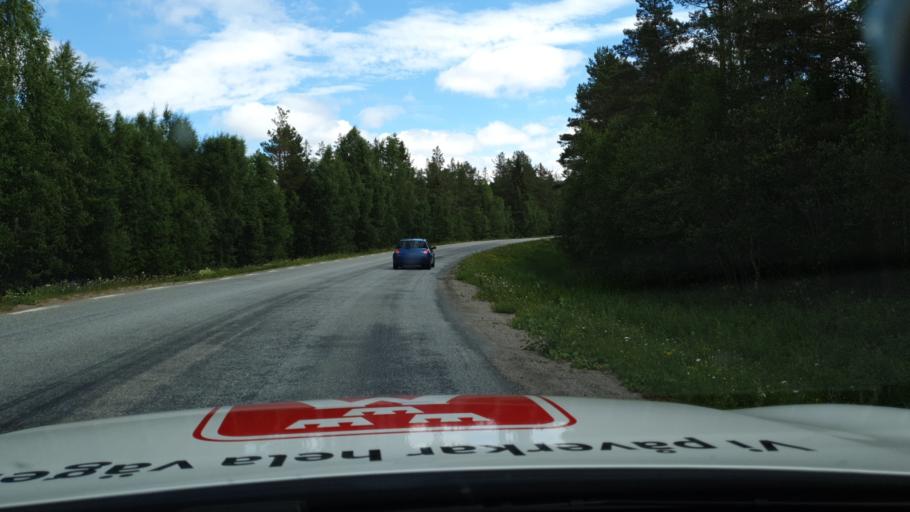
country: SE
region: Jaemtland
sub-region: Braecke Kommun
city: Braecke
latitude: 62.7804
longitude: 15.4658
